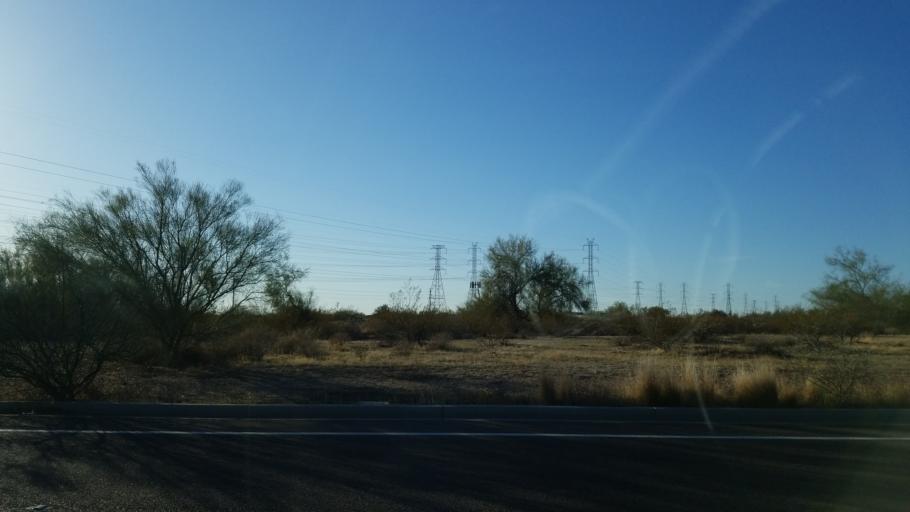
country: US
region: Arizona
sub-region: Maricopa County
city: Paradise Valley
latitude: 33.6509
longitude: -111.8878
